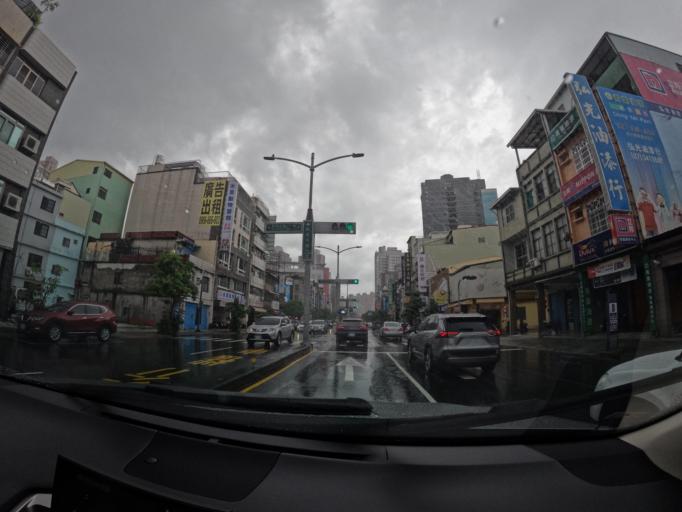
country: TW
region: Kaohsiung
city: Kaohsiung
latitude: 22.6698
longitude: 120.3055
